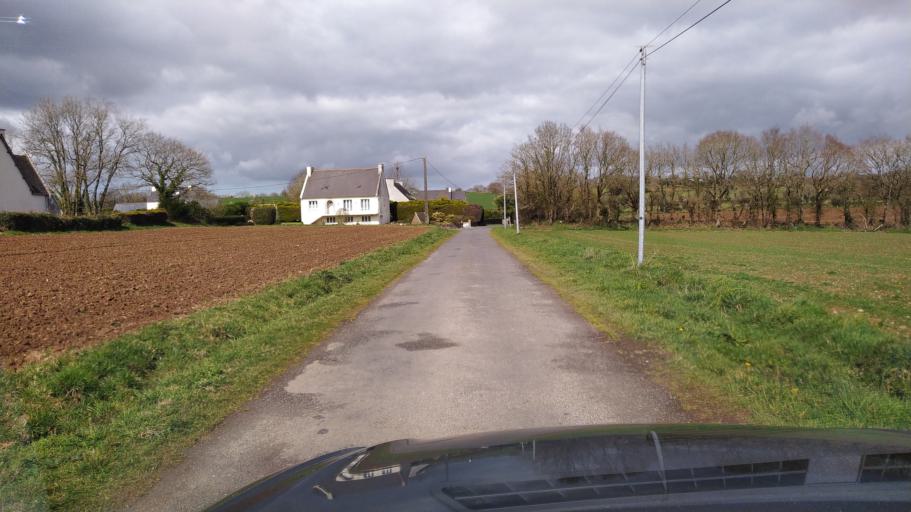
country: FR
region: Brittany
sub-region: Departement du Finistere
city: Bodilis
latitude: 48.5181
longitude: -4.1195
